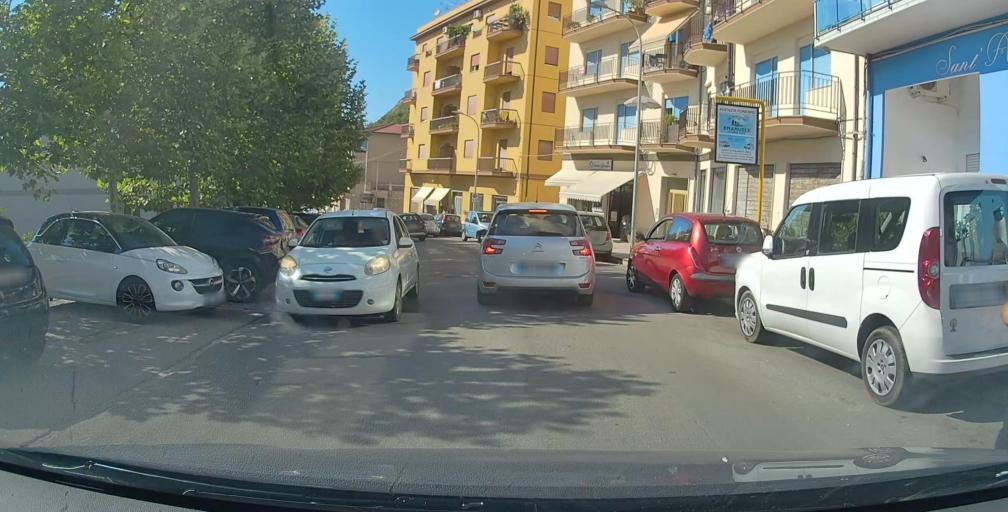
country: IT
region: Sicily
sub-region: Messina
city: Capo d'Orlando
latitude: 38.1622
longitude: 14.7486
